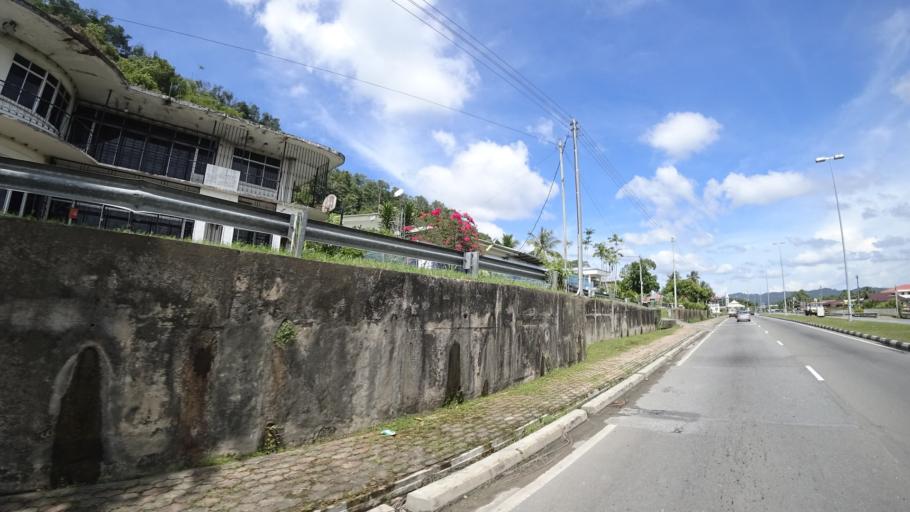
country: BN
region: Brunei and Muara
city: Bandar Seri Begawan
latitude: 4.8524
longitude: 114.8815
